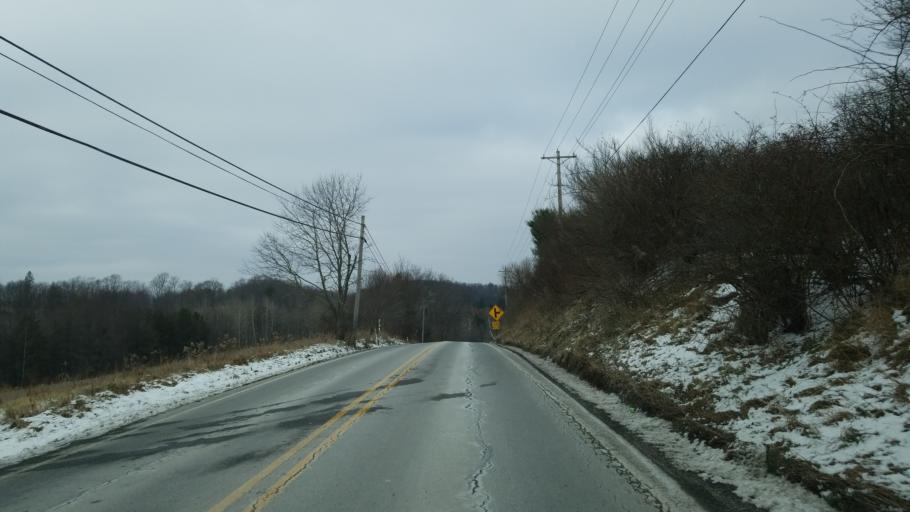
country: US
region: Pennsylvania
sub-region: Clearfield County
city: DuBois
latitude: 41.0865
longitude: -78.7366
